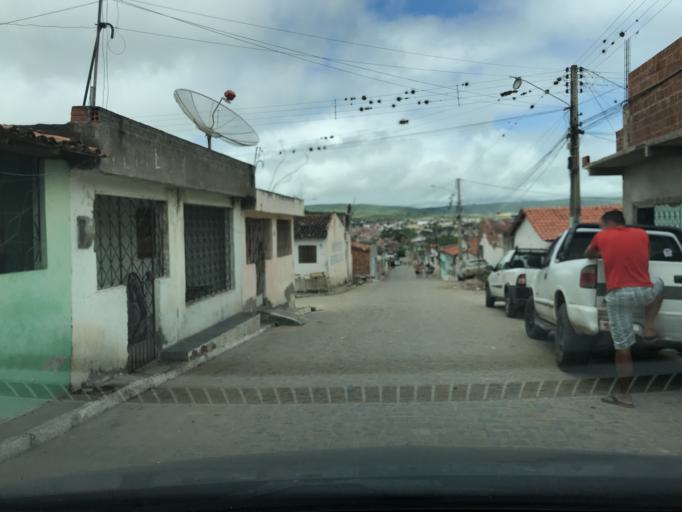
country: BR
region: Pernambuco
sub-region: Bezerros
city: Bezerros
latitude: -8.2290
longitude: -35.7625
